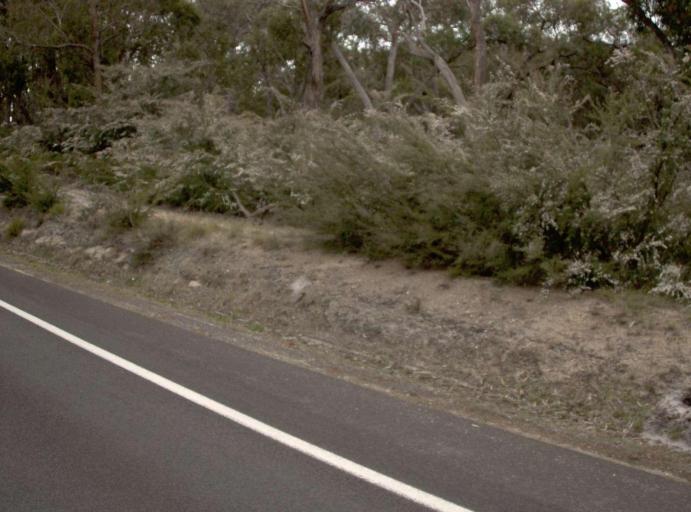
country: AU
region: Victoria
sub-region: Wellington
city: Sale
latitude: -38.3344
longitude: 147.0150
